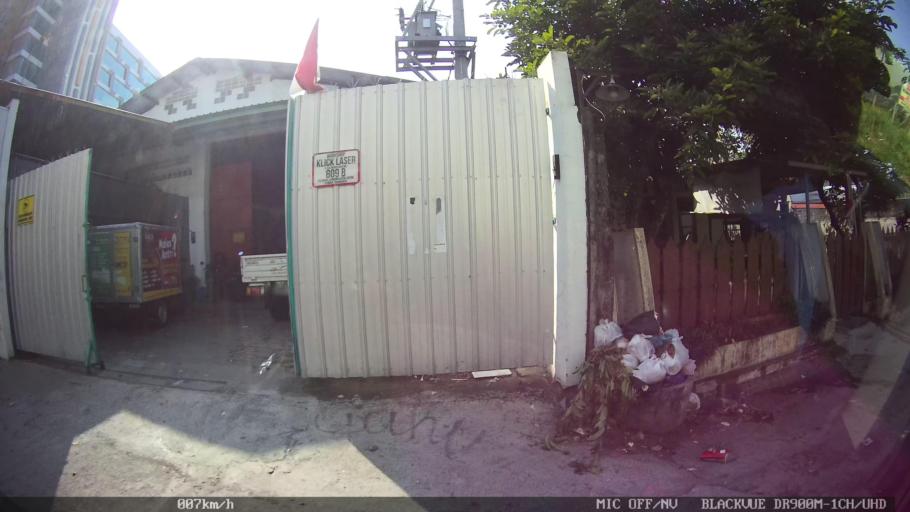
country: ID
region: Daerah Istimewa Yogyakarta
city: Depok
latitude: -7.7626
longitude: 110.3976
